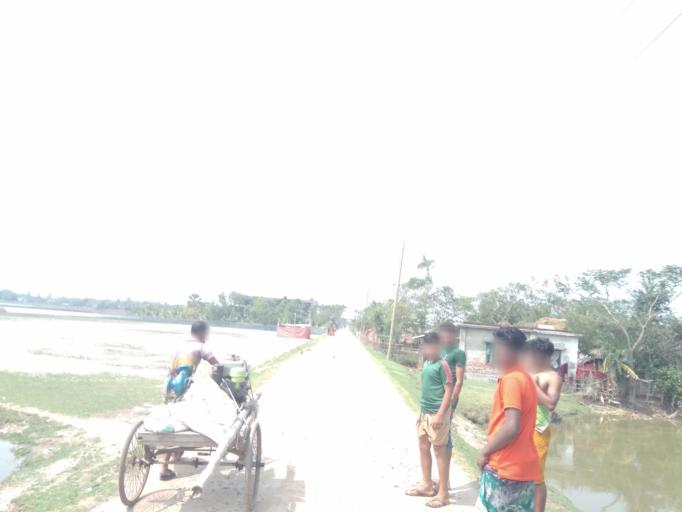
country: IN
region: West Bengal
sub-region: North 24 Parganas
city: Taki
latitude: 22.3029
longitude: 89.2677
